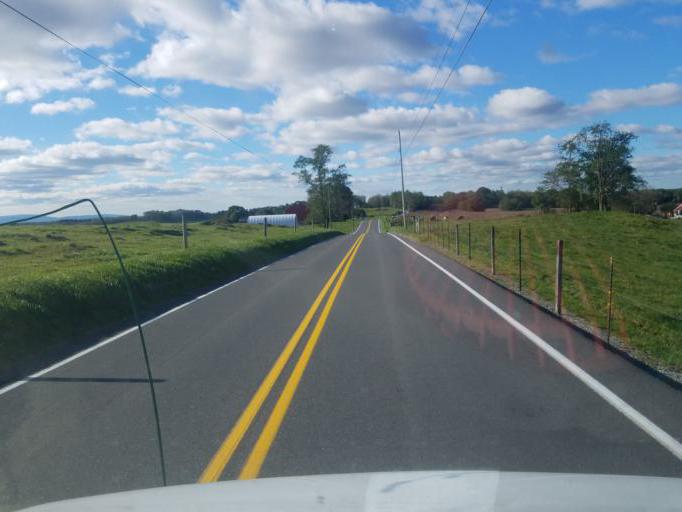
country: US
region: Pennsylvania
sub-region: Franklin County
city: Guilford Siding
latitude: 39.8128
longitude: -77.6457
